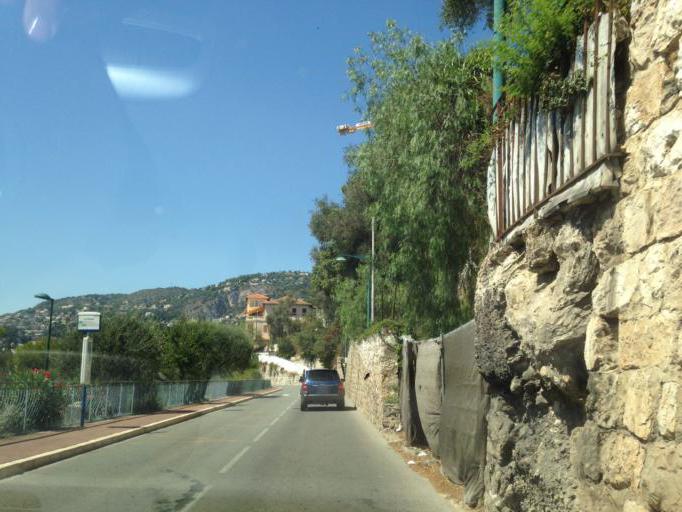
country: FR
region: Provence-Alpes-Cote d'Azur
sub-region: Departement des Alpes-Maritimes
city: Saint-Jean-Cap-Ferrat
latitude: 43.6963
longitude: 7.3276
